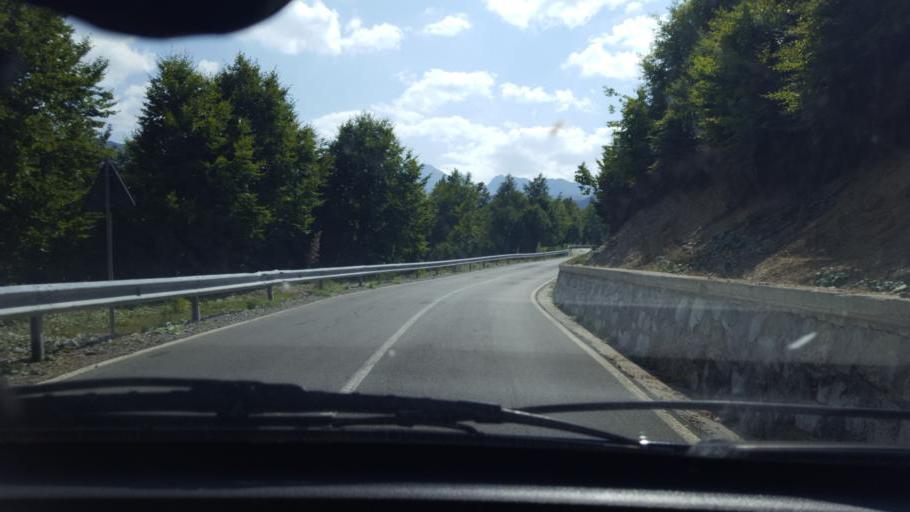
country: AL
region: Kukes
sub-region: Rrethi i Tropojes
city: Valbone
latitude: 42.5380
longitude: 19.7205
